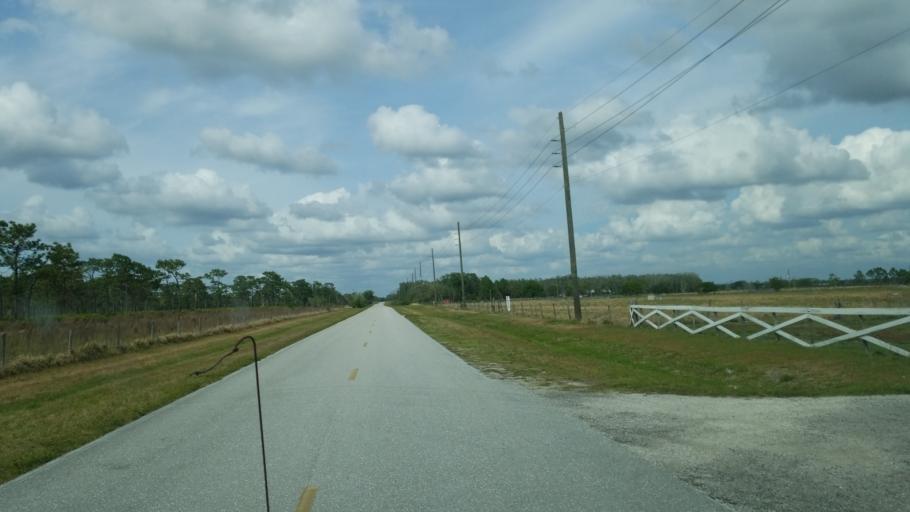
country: US
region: Florida
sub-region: Okeechobee County
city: Cypress Quarters
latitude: 27.5018
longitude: -80.7751
